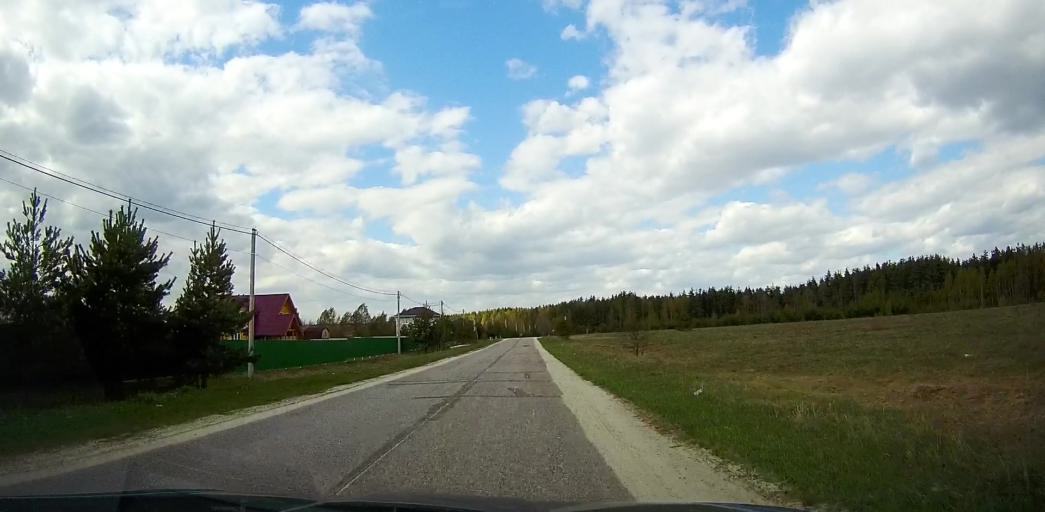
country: RU
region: Moskovskaya
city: Davydovo
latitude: 55.6407
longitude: 38.7763
